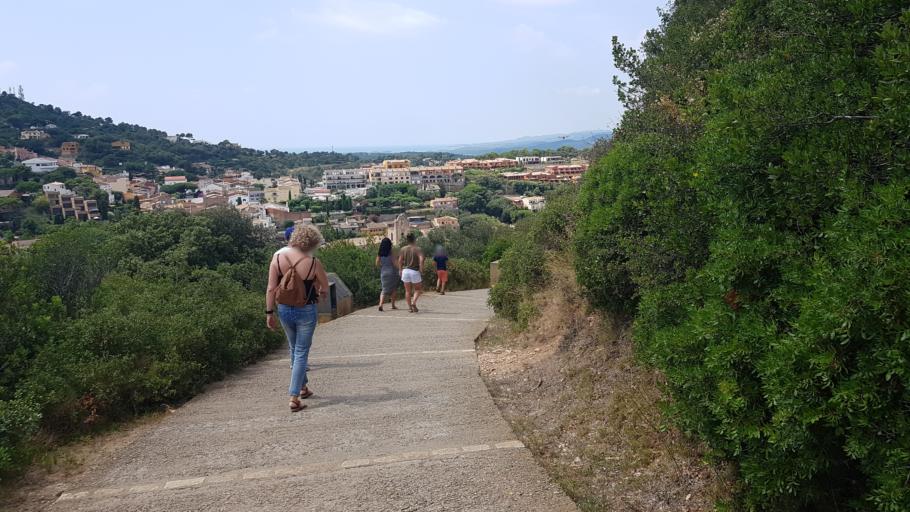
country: ES
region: Catalonia
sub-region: Provincia de Girona
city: Begur
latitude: 41.9564
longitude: 3.2089
